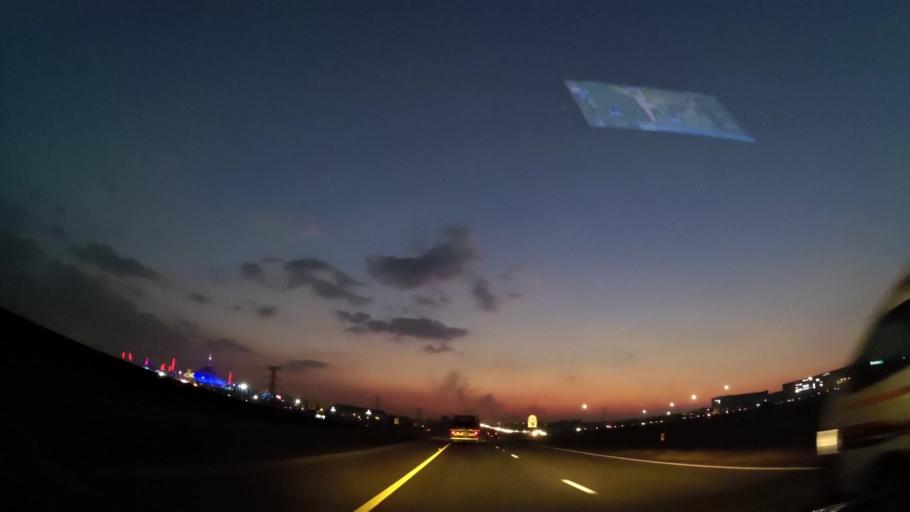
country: ZA
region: Gauteng
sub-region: Ekurhuleni Metropolitan Municipality
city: Brakpan
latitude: -26.2554
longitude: 28.3211
